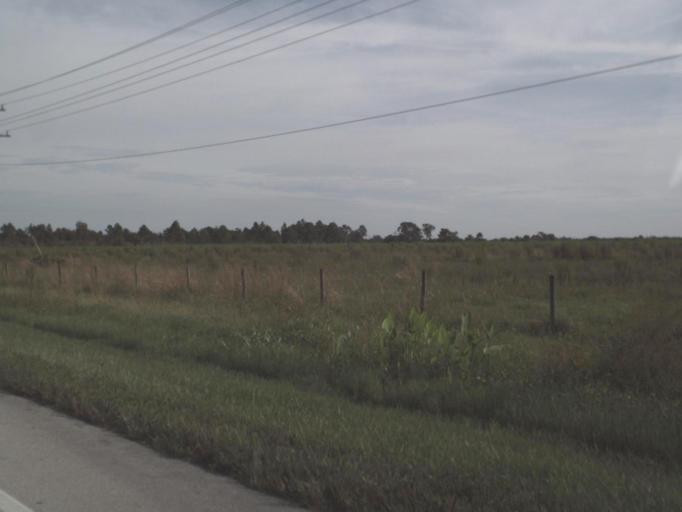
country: US
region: Florida
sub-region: Lee County
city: Fort Myers Shores
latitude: 26.7486
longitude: -81.7609
